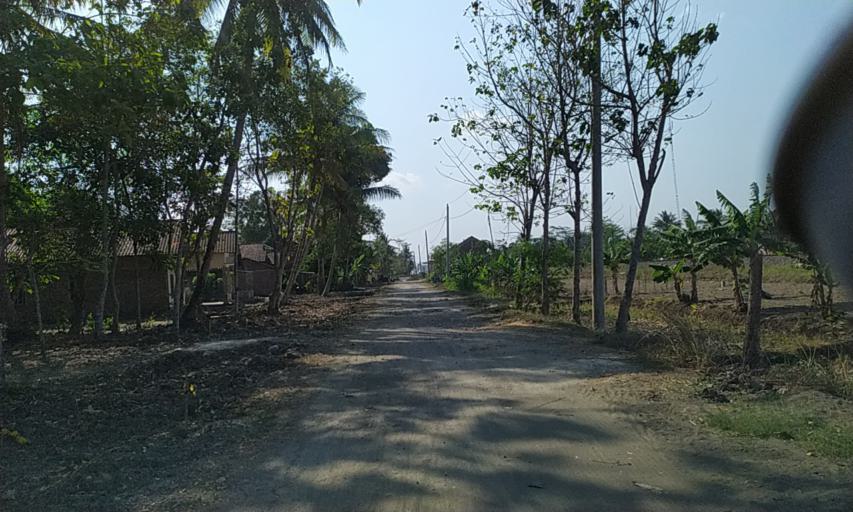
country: ID
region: Central Java
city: Alurbulu
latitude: -7.5014
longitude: 108.8298
